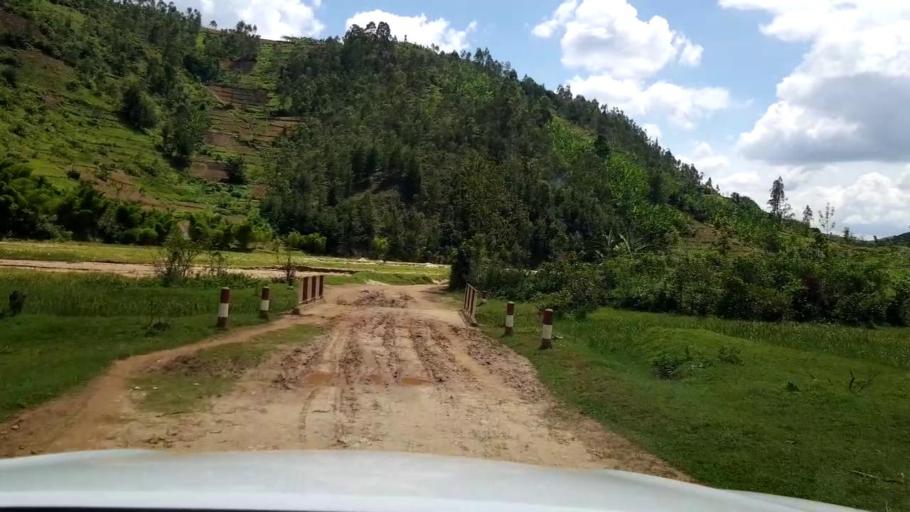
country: RW
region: Southern Province
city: Gitarama
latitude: -2.0090
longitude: 29.6184
